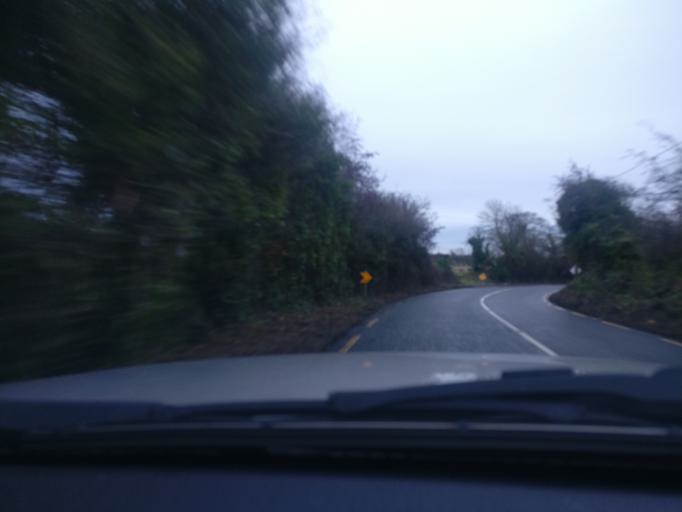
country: IE
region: Leinster
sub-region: Kildare
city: Kilcock
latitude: 53.4529
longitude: -6.6234
